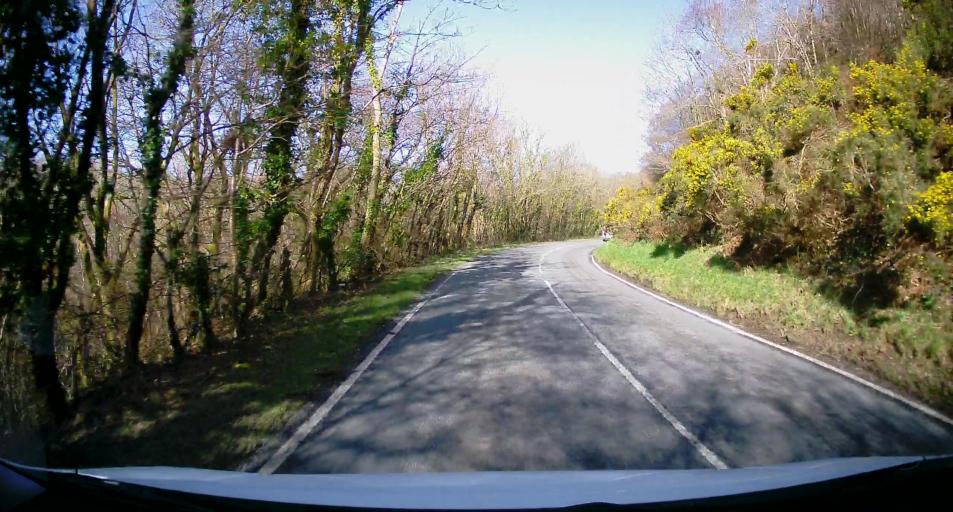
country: GB
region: Wales
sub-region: County of Ceredigion
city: Llanarth
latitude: 52.1978
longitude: -4.3177
